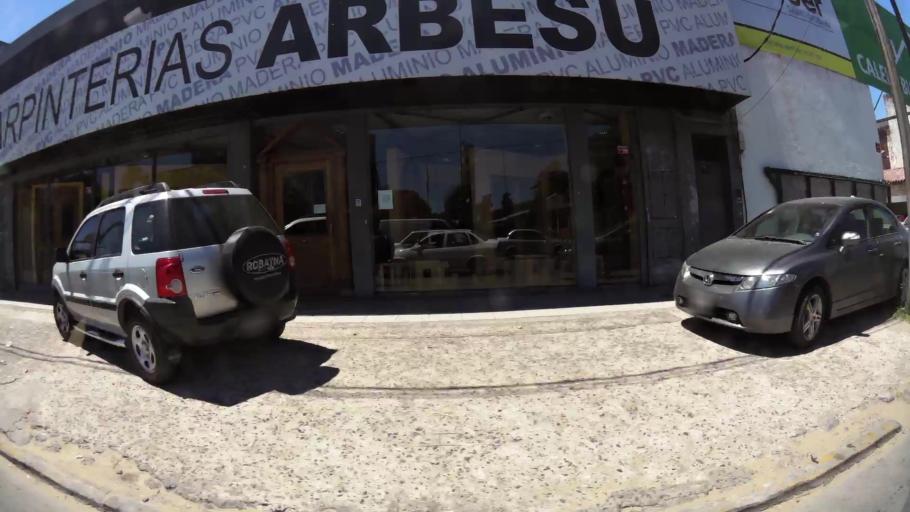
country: AR
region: Buenos Aires
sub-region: Partido de San Isidro
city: San Isidro
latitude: -34.5032
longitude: -58.5613
